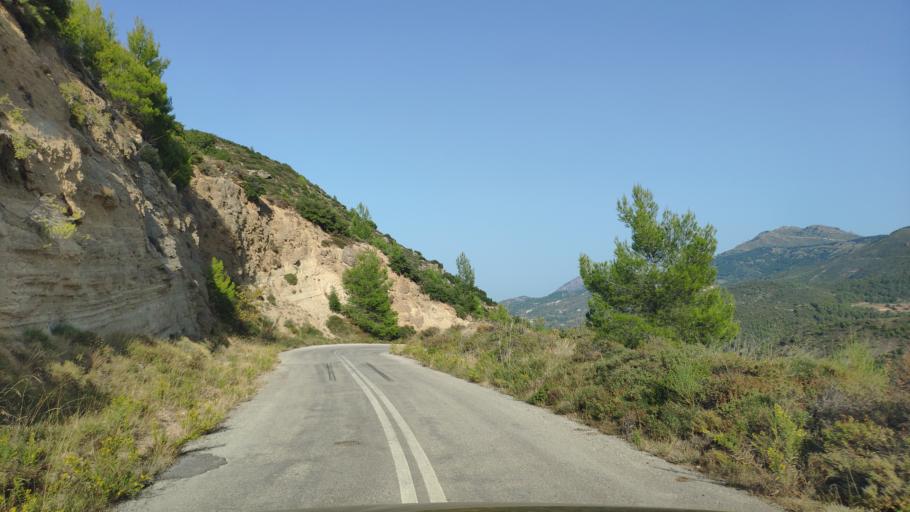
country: GR
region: West Greece
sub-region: Nomos Achaias
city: Aiyira
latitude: 38.0680
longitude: 22.3863
